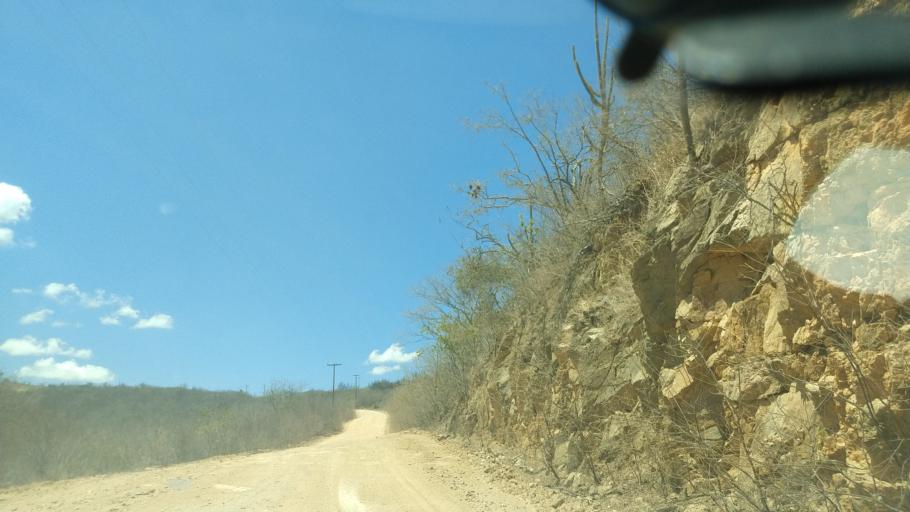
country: BR
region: Rio Grande do Norte
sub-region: Cerro Cora
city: Cerro Cora
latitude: -6.0108
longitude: -36.3205
